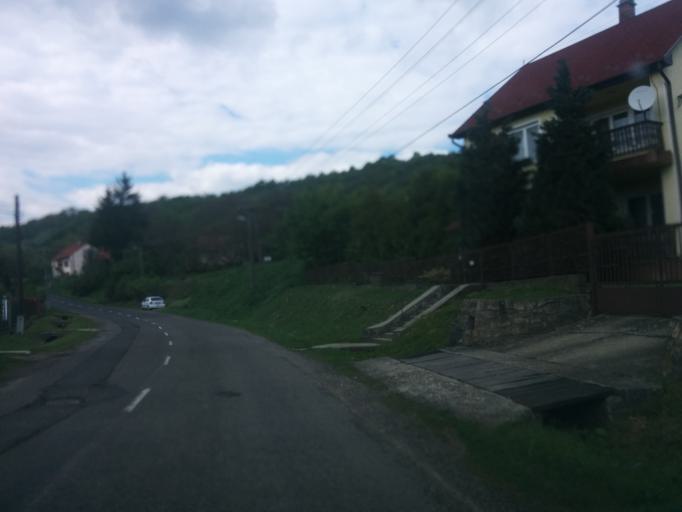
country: HU
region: Nograd
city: Romhany
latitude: 47.8791
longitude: 19.2394
